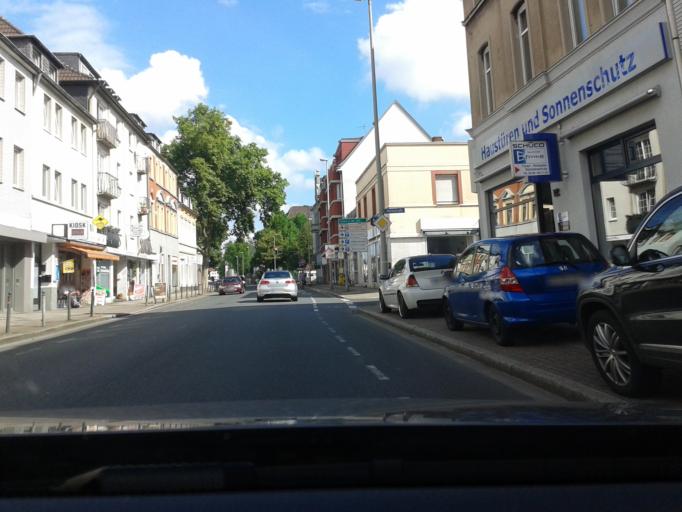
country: DE
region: North Rhine-Westphalia
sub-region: Regierungsbezirk Dusseldorf
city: Oberhausen
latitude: 51.4632
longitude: 6.8524
